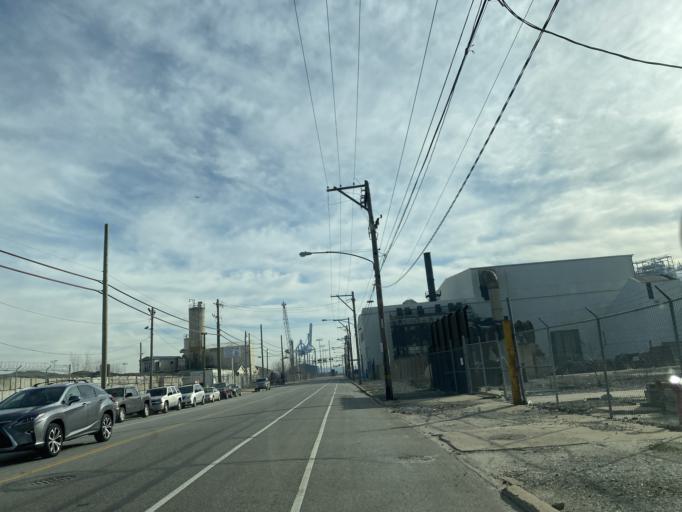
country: US
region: New Jersey
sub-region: Camden County
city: Pennsauken
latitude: 39.9850
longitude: -75.0861
